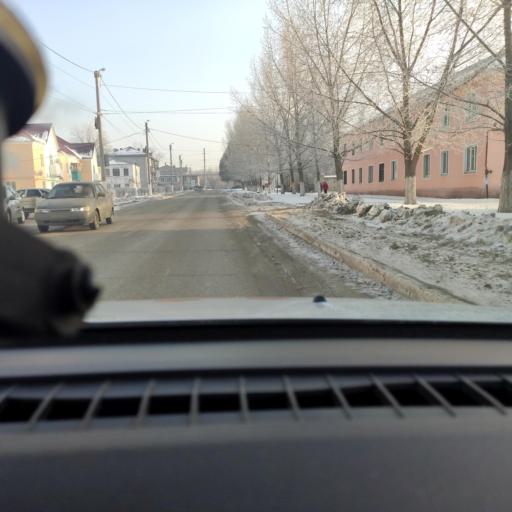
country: RU
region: Samara
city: Chapayevsk
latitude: 52.9728
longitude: 49.7031
